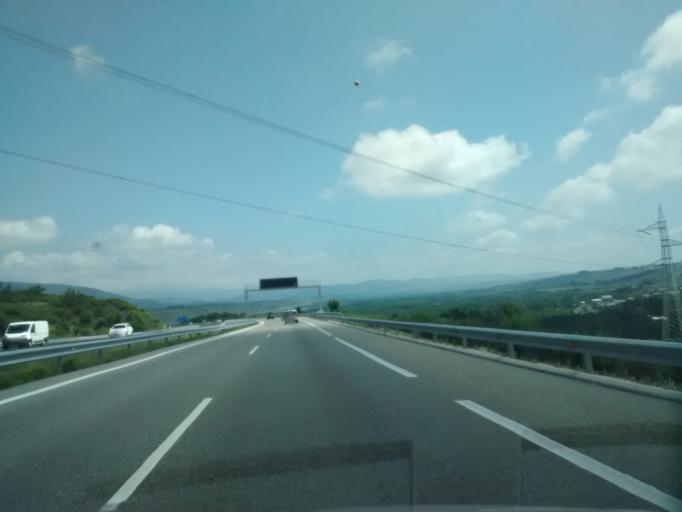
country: ES
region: Castille and Leon
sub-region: Provincia de Leon
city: Molinaseca
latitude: 42.5756
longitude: -6.5334
